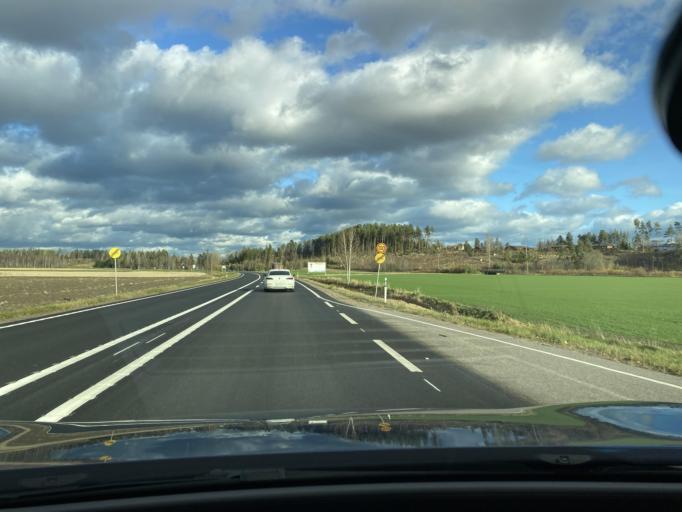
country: FI
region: Haeme
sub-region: Riihimaeki
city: Oitti
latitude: 60.7967
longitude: 25.0245
